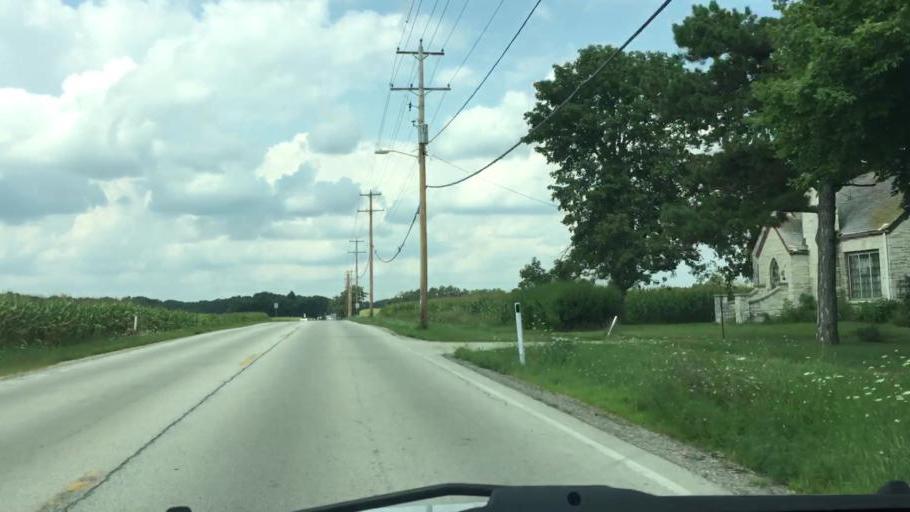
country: US
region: Wisconsin
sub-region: Waukesha County
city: North Prairie
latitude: 42.9388
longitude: -88.4056
